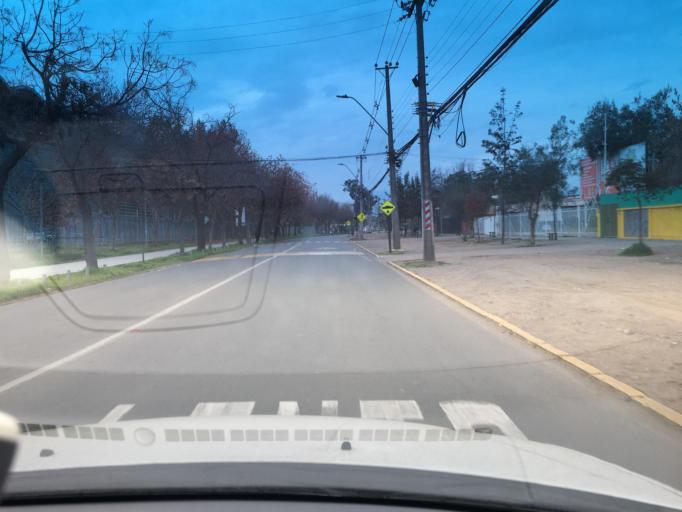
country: CL
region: Santiago Metropolitan
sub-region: Provincia de Santiago
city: Villa Presidente Frei, Nunoa, Santiago, Chile
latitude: -33.4669
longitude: -70.6067
